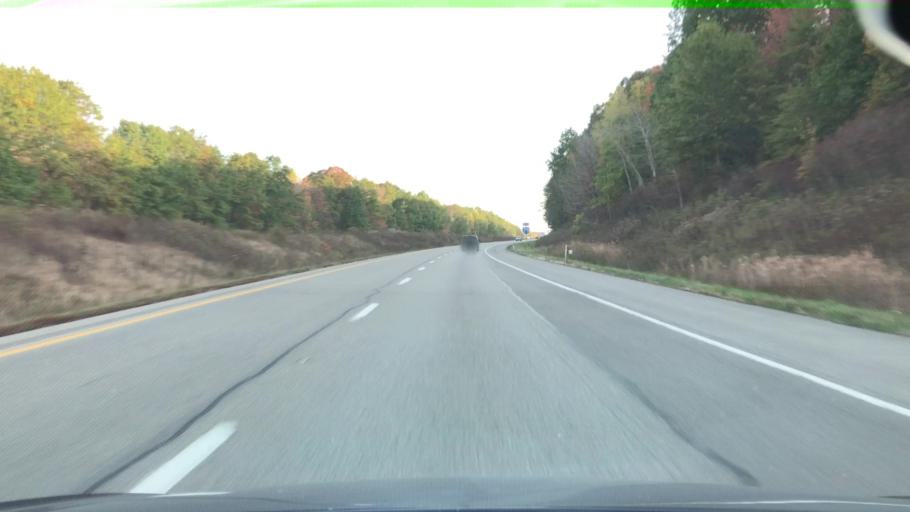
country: US
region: Pennsylvania
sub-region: Mercer County
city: Mercer
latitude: 41.2678
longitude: -80.1658
